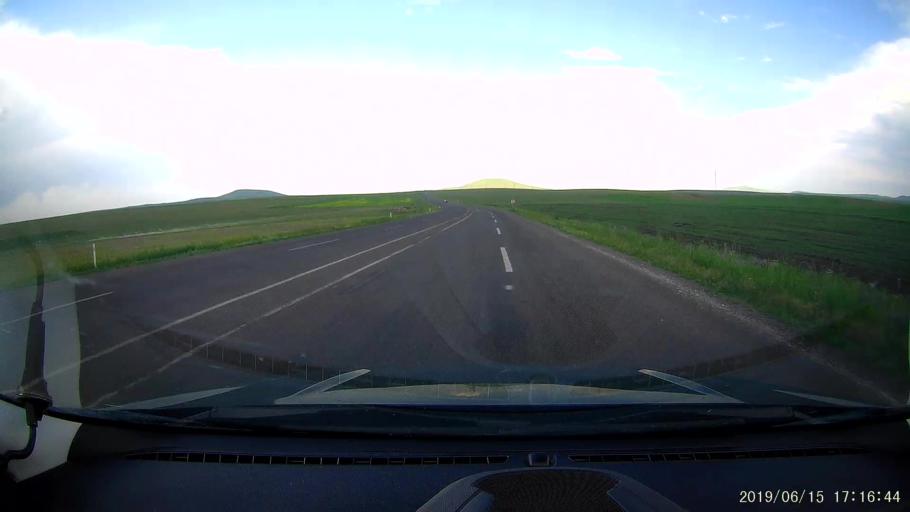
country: TR
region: Kars
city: Kars
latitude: 40.6143
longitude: 43.2235
